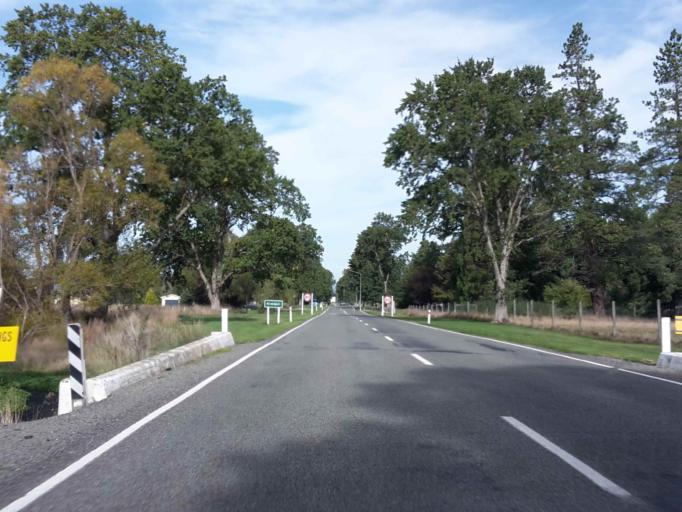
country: NZ
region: Canterbury
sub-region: Timaru District
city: Pleasant Point
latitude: -44.0411
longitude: 170.7536
